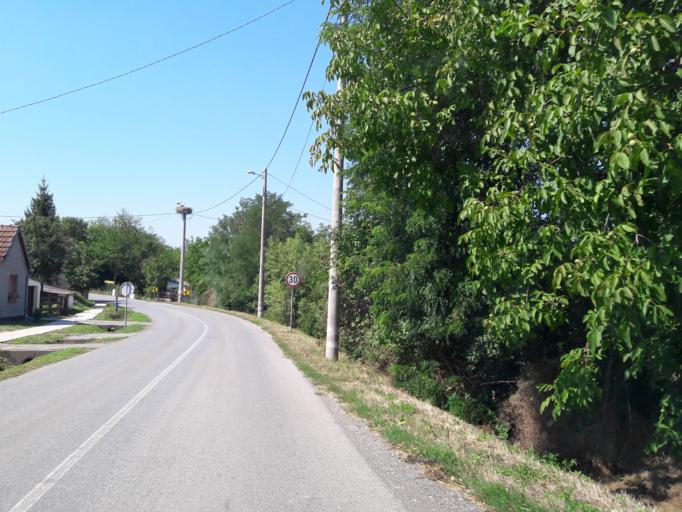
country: HR
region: Osjecko-Baranjska
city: Gorjani
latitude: 45.3729
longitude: 18.4085
